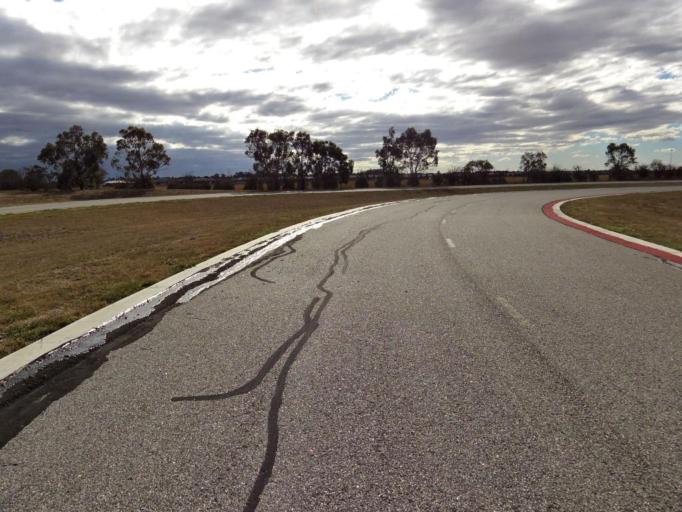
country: AU
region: Victoria
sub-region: Casey
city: Junction Village
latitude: -38.1276
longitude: 145.3115
